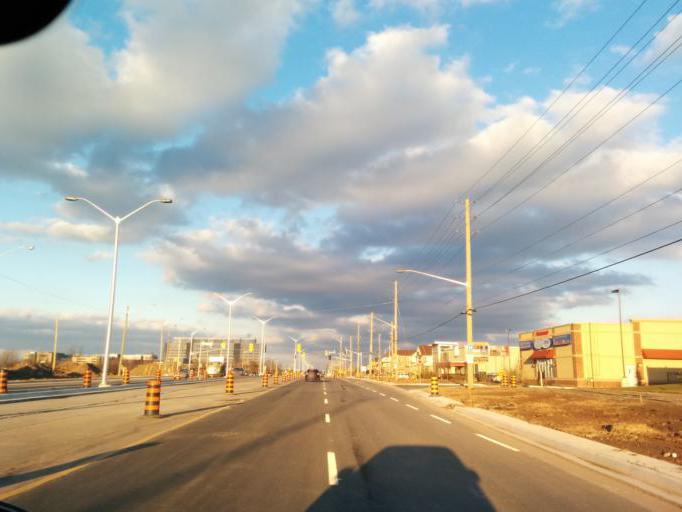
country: CA
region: Ontario
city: Oakville
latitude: 43.4424
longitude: -79.7693
